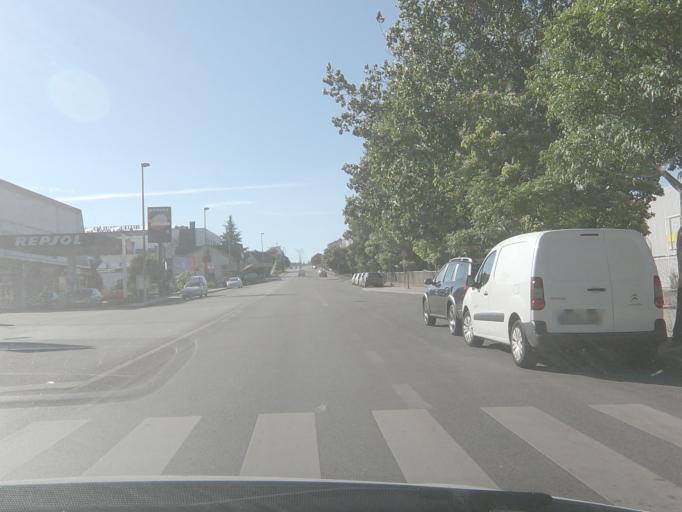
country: PT
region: Viseu
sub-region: Viseu
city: Abraveses
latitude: 40.6722
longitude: -7.9200
